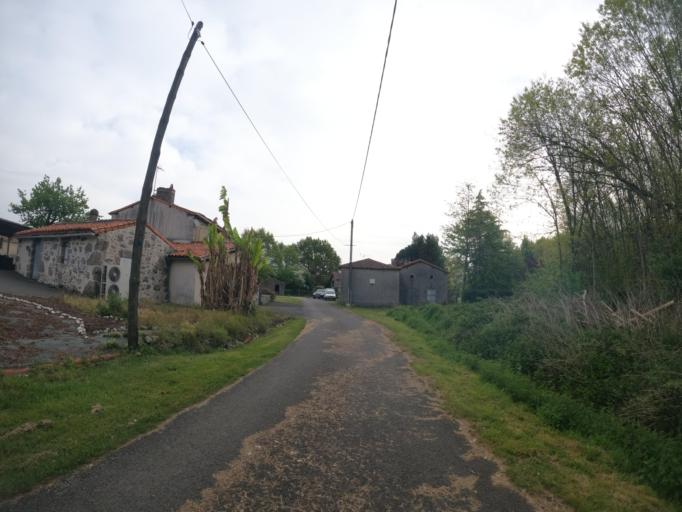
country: FR
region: Poitou-Charentes
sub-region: Departement des Deux-Sevres
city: La Chapelle-Saint-Laurent
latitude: 46.6976
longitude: -0.4891
